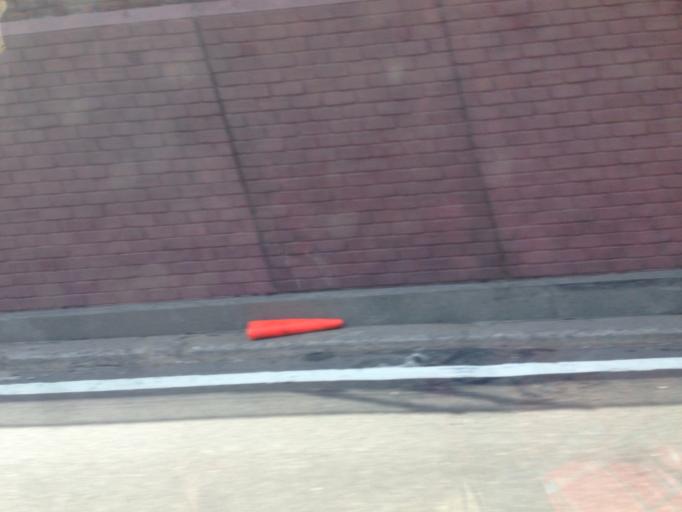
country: US
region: New York
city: New York City
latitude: 40.6826
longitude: -74.0023
